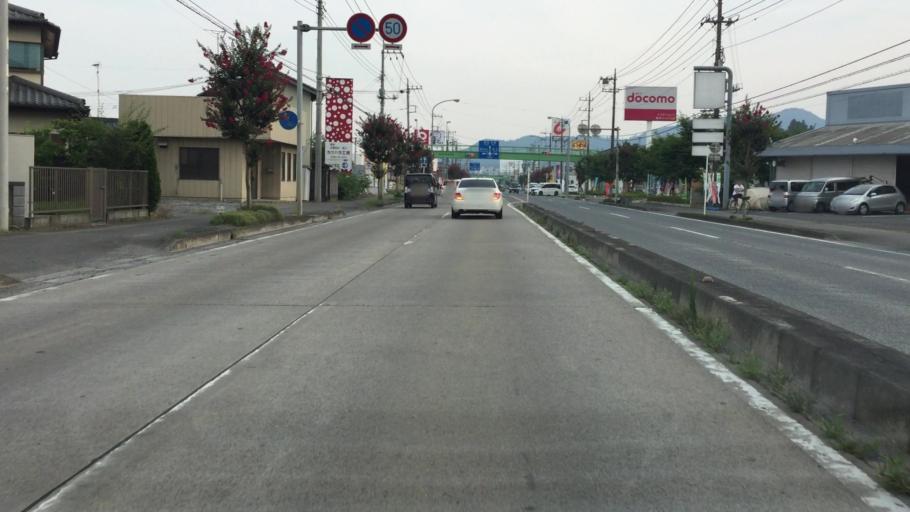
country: JP
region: Tochigi
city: Tochigi
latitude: 36.3883
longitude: 139.7199
